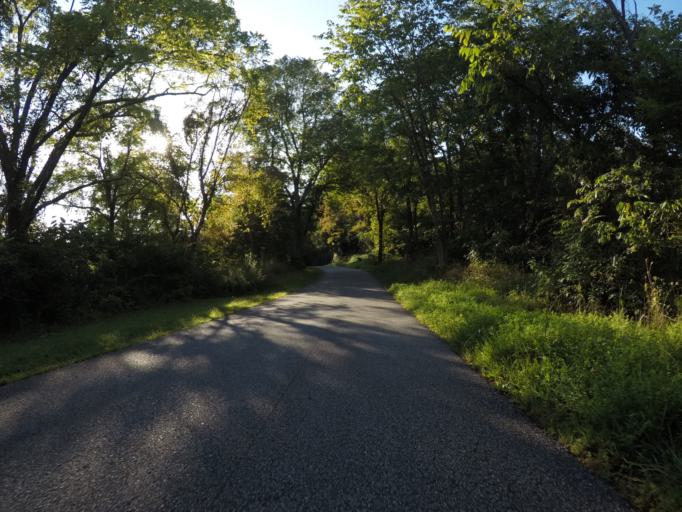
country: US
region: Ohio
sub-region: Lawrence County
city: Coal Grove
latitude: 38.5976
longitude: -82.5525
